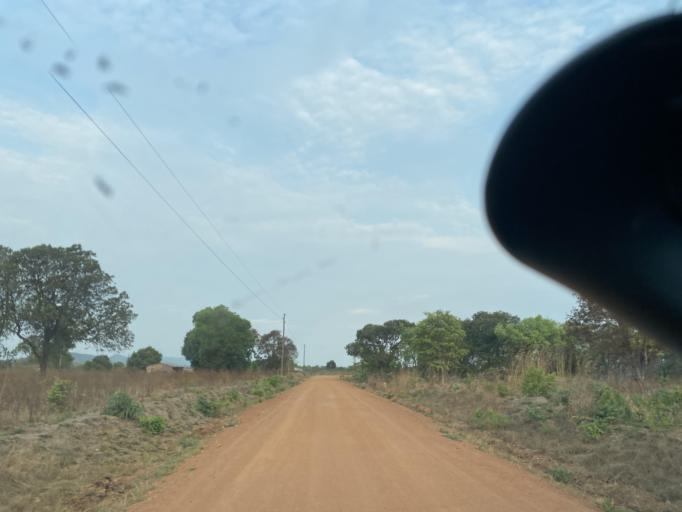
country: ZM
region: Lusaka
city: Chongwe
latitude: -15.1943
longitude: 28.5801
